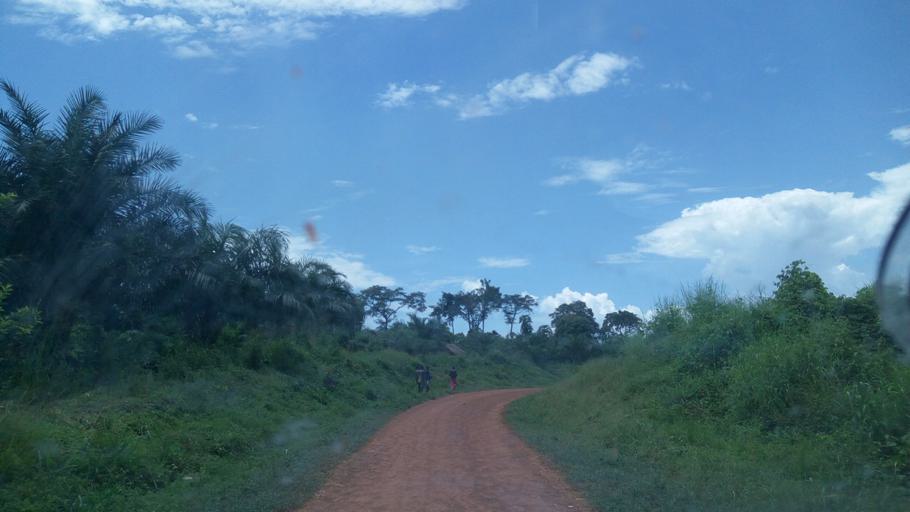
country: TZ
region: Kigoma
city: Kigoma
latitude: -4.9480
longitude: 28.7427
